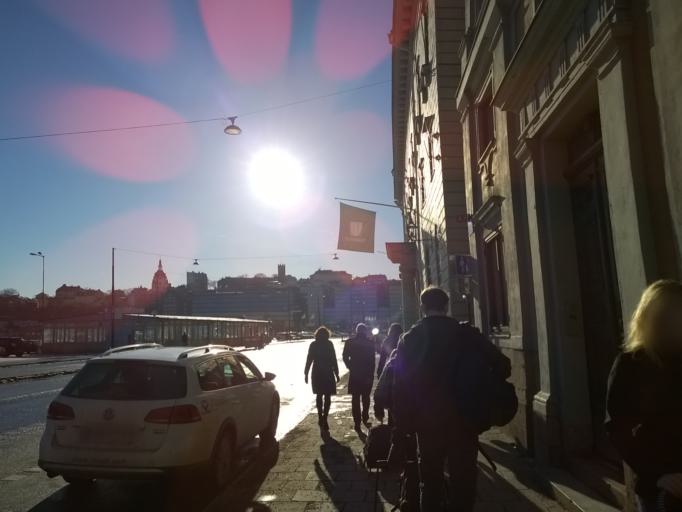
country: SE
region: Stockholm
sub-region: Stockholms Kommun
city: Stockholm
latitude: 59.3235
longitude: 18.0750
